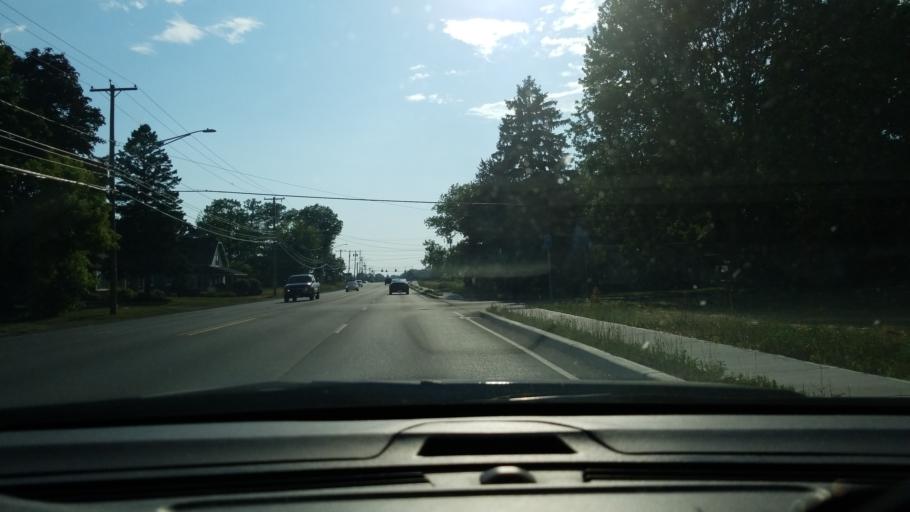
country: US
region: New York
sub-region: Onondaga County
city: North Syracuse
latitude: 43.1223
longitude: -76.1519
